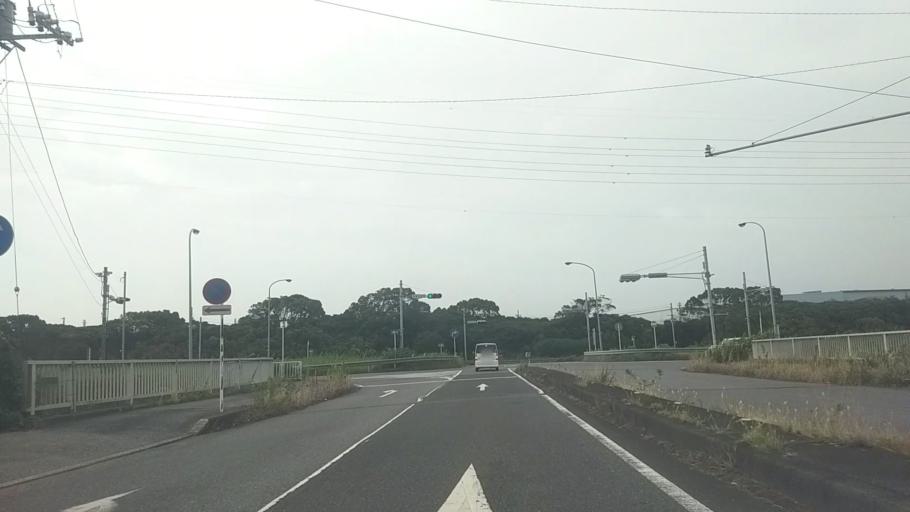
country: JP
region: Chiba
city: Kimitsu
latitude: 35.3470
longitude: 139.8899
